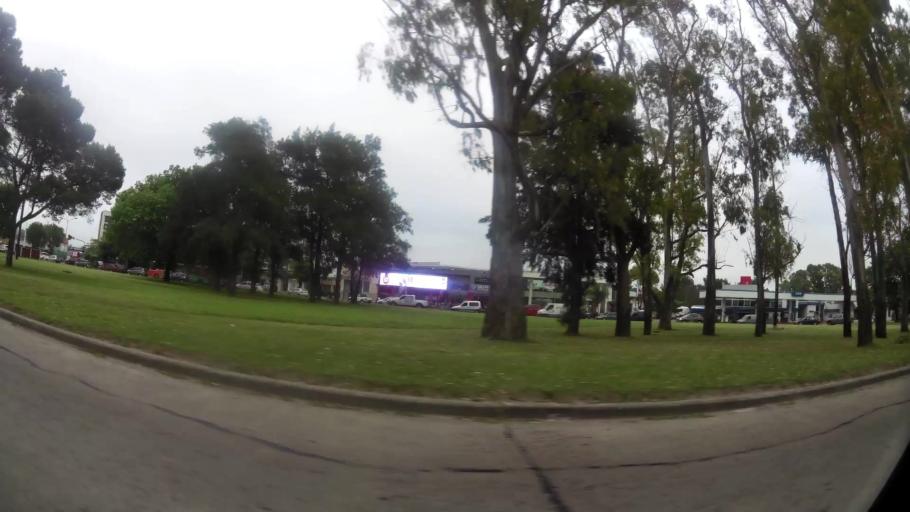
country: AR
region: Buenos Aires
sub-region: Partido de La Plata
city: La Plata
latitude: -34.9221
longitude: -57.9899
